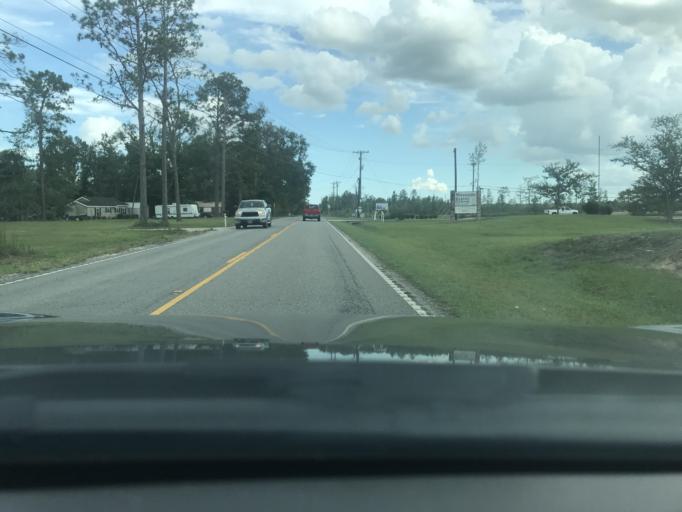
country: US
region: Louisiana
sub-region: Calcasieu Parish
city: Moss Bluff
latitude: 30.3235
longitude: -93.2582
